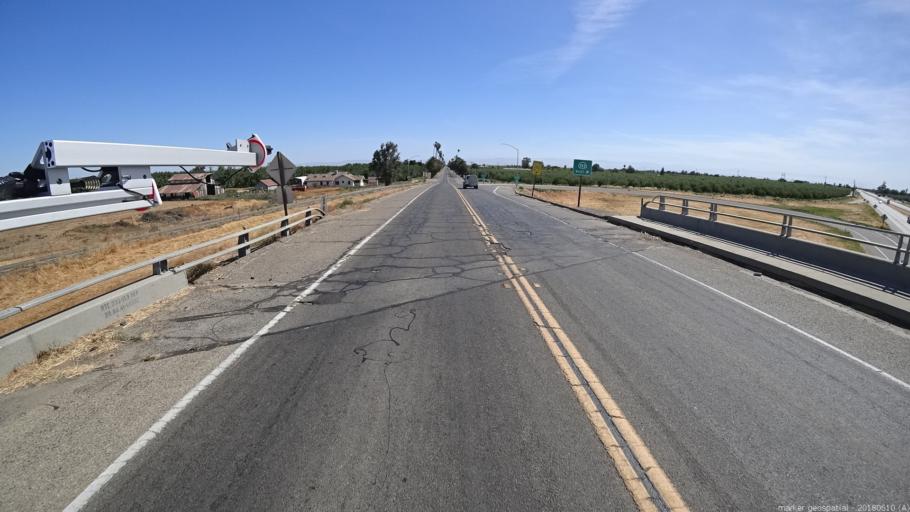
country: US
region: California
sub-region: Madera County
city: Chowchilla
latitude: 37.0839
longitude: -120.2971
